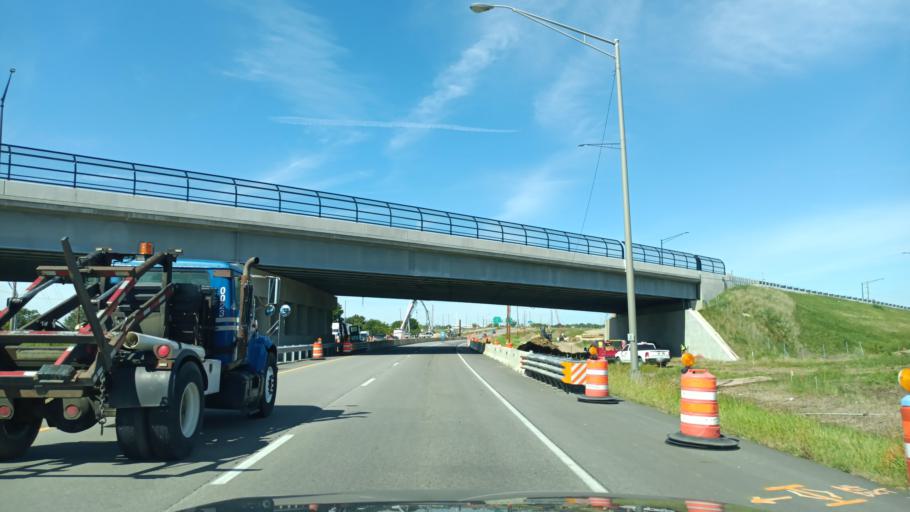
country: US
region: Illinois
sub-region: Champaign County
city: Champaign
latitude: 40.1411
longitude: -88.2760
